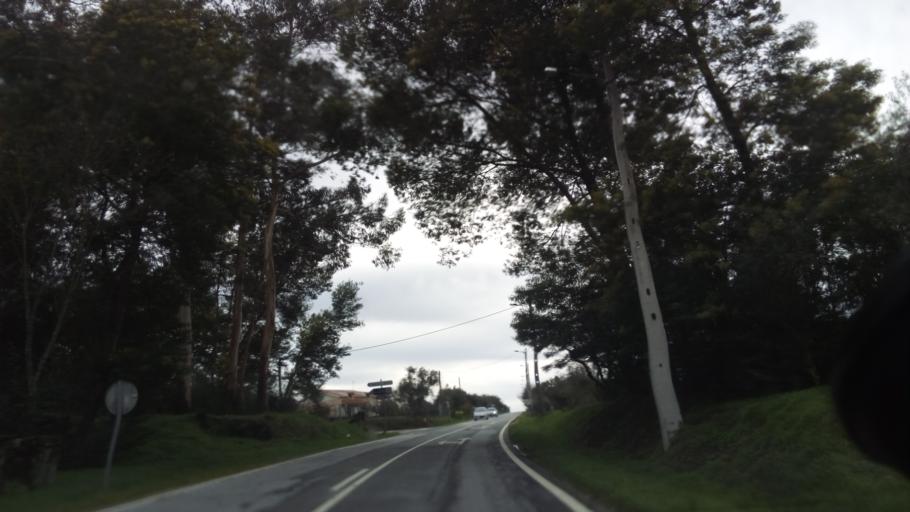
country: PT
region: Guarda
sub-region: Seia
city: Seia
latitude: 40.4804
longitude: -7.6654
